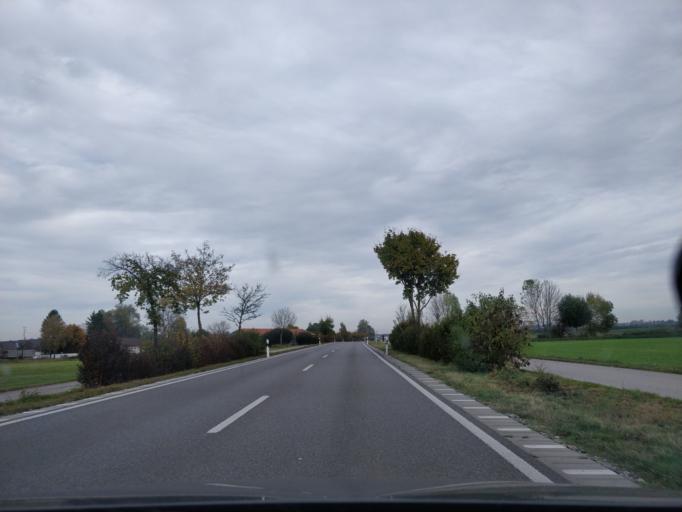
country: DE
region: Bavaria
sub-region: Swabia
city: Mering
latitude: 48.2677
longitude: 10.9486
